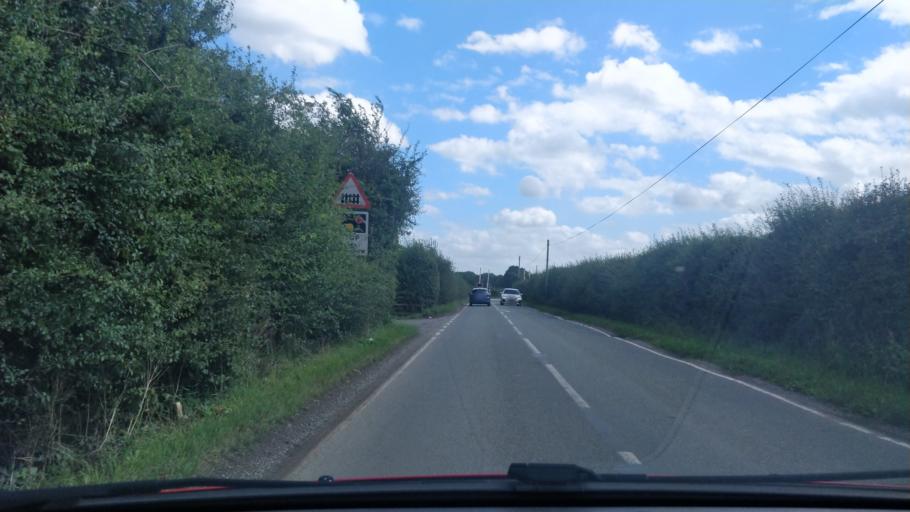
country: GB
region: Wales
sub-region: Wrexham
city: Rossett
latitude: 53.1536
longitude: -2.9382
